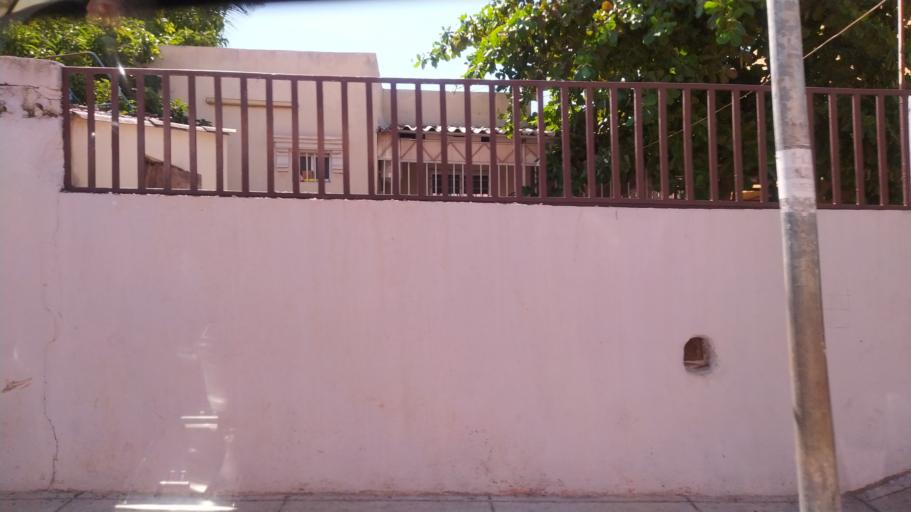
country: AO
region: Luanda
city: Luanda
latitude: -8.8462
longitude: 13.2294
